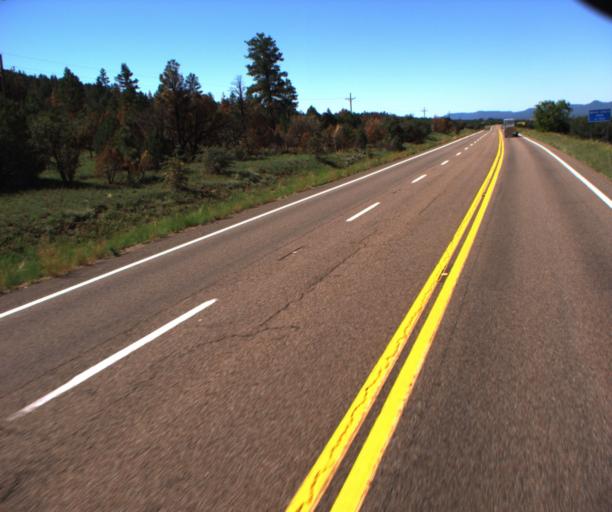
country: US
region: Arizona
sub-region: Navajo County
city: Linden
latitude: 34.0499
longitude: -110.2214
